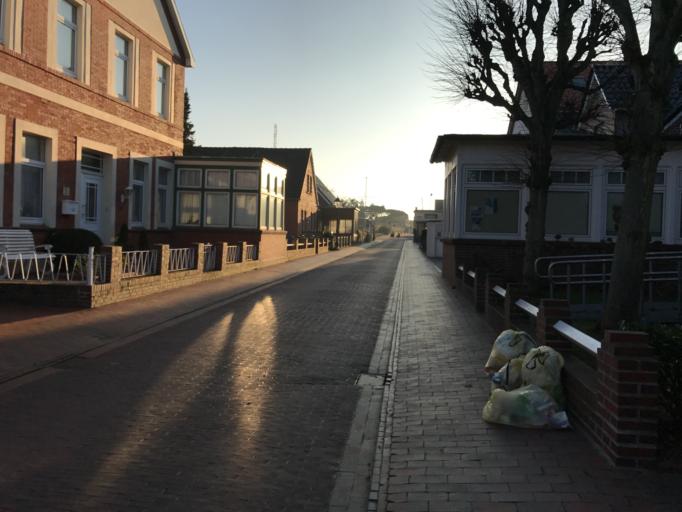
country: DE
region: Lower Saxony
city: Borkum
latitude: 53.5833
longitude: 6.6686
